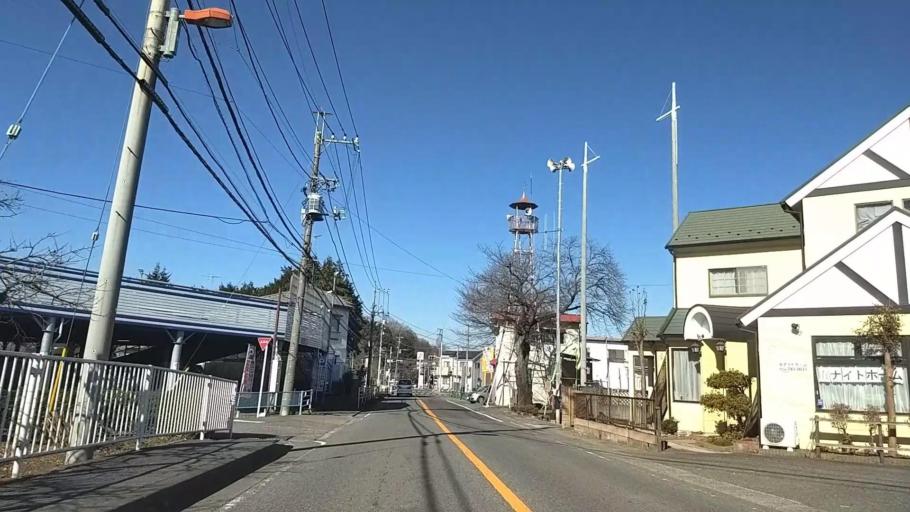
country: JP
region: Tokyo
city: Hachioji
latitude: 35.6024
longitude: 139.3009
